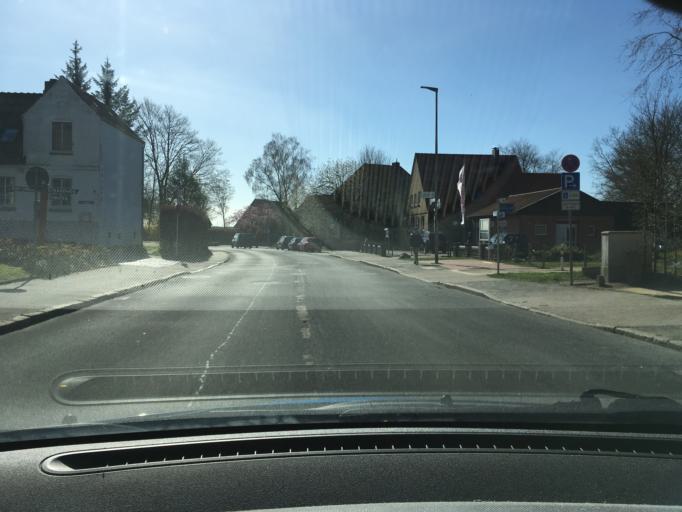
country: DE
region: Schleswig-Holstein
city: Schleswig
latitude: 54.5133
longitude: 9.5671
